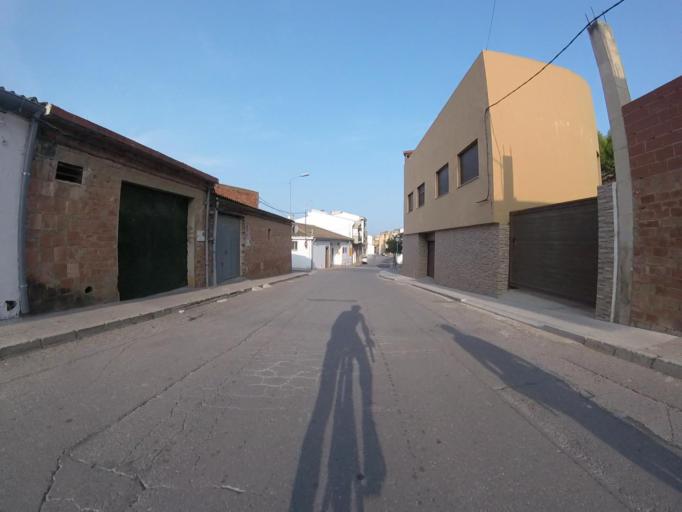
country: ES
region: Valencia
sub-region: Provincia de Castello
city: Cabanes
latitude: 40.1543
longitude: 0.0458
